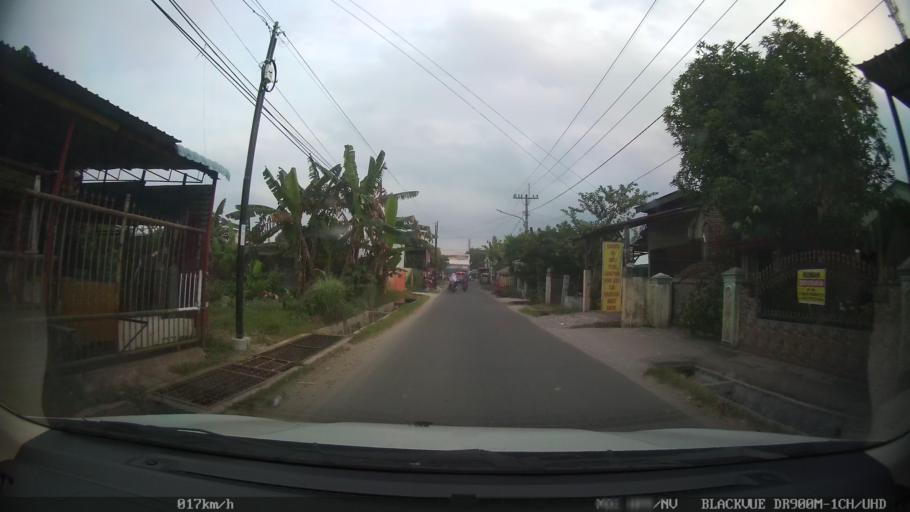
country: ID
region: North Sumatra
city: Sunggal
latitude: 3.5649
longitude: 98.6040
